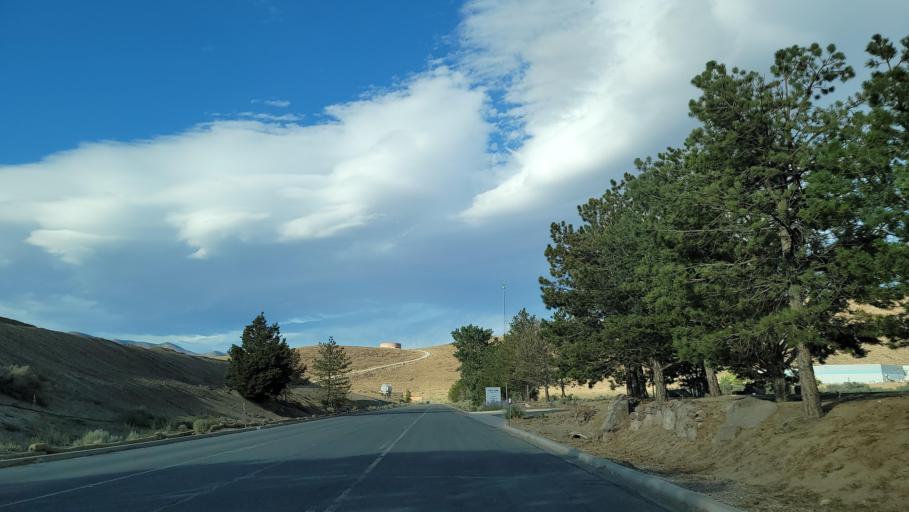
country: US
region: Nevada
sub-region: Washoe County
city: Spanish Springs
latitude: 39.5494
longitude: -119.5446
